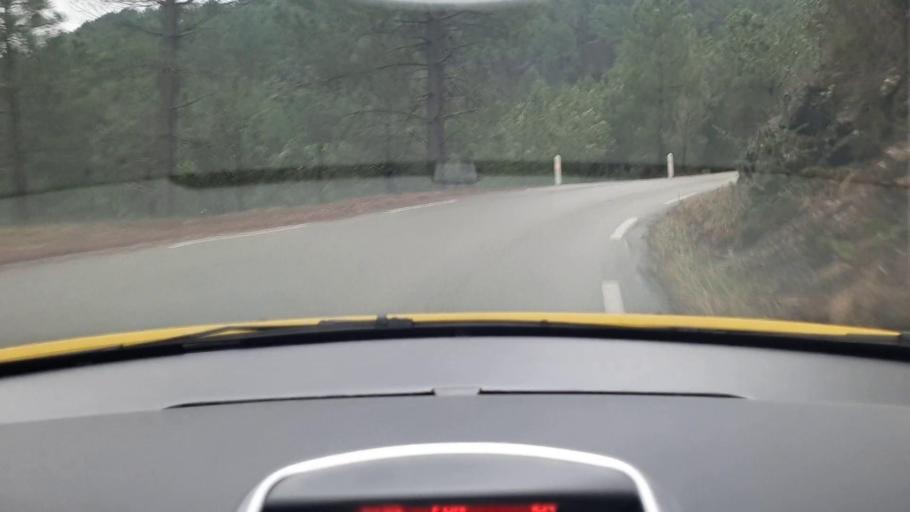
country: FR
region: Languedoc-Roussillon
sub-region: Departement du Gard
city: Besseges
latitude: 44.2767
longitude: 4.0751
